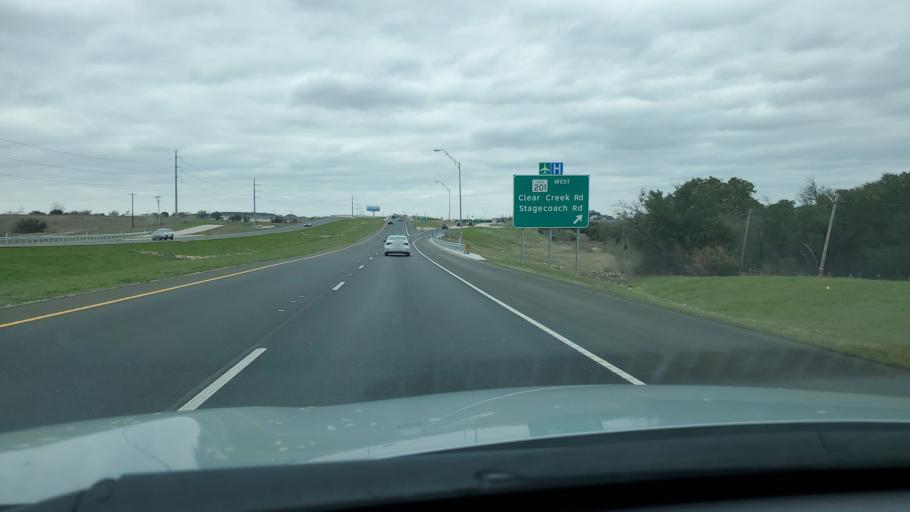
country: US
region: Texas
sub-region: Bell County
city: Killeen
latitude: 31.0530
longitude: -97.7639
